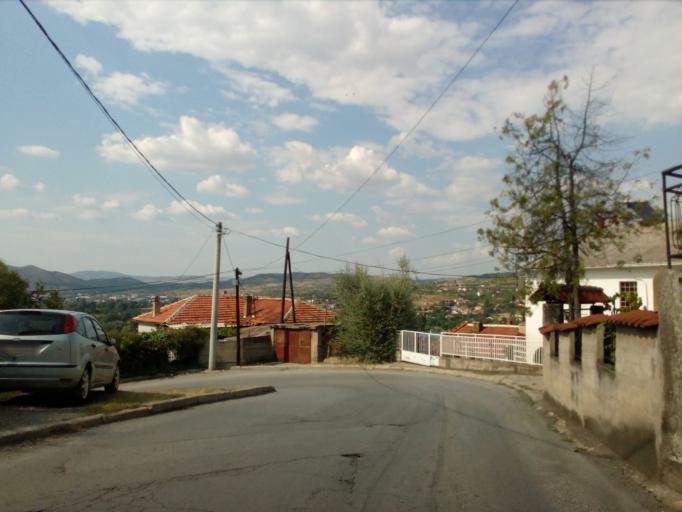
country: MK
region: Veles
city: Veles
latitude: 41.7162
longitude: 21.7779
